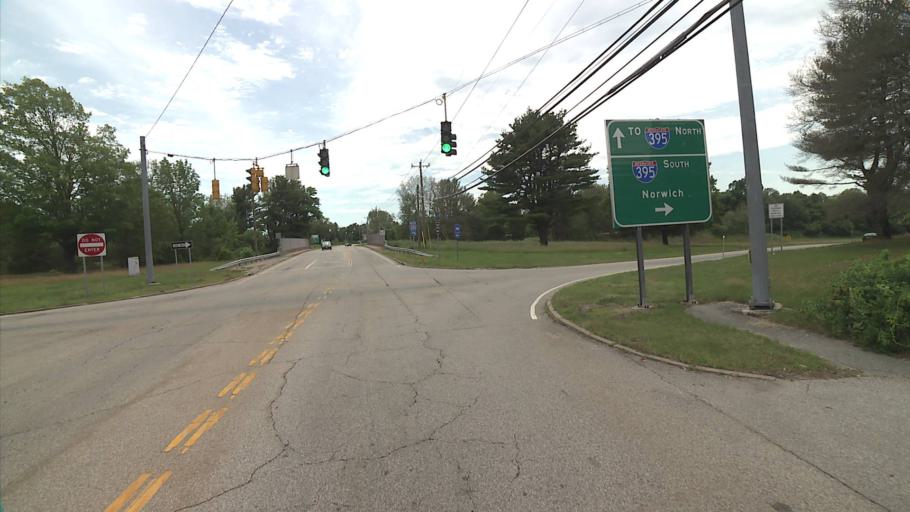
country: US
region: Connecticut
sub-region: New London County
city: Jewett City
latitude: 41.5917
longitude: -71.9762
